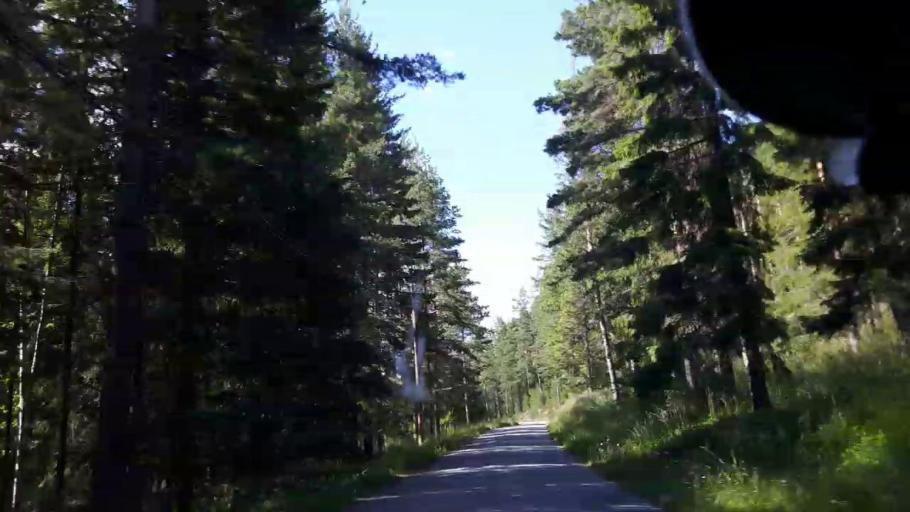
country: SE
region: Jaemtland
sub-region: Braecke Kommun
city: Braecke
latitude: 62.8587
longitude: 15.2784
